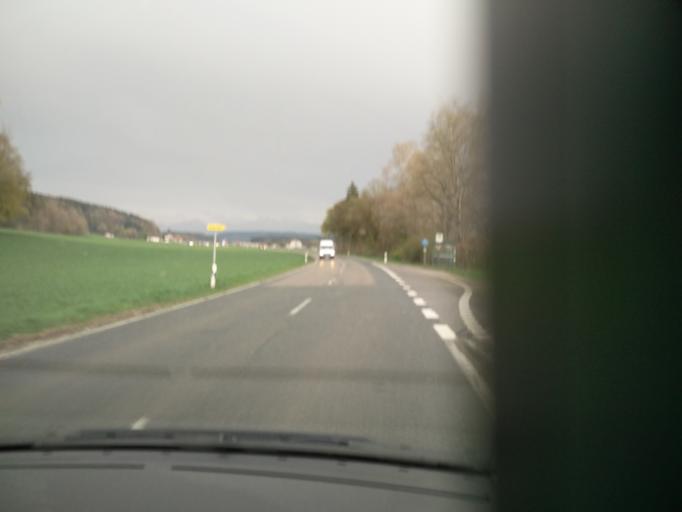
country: DE
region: Bavaria
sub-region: Upper Bavaria
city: Halfing
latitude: 47.9377
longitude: 12.2809
